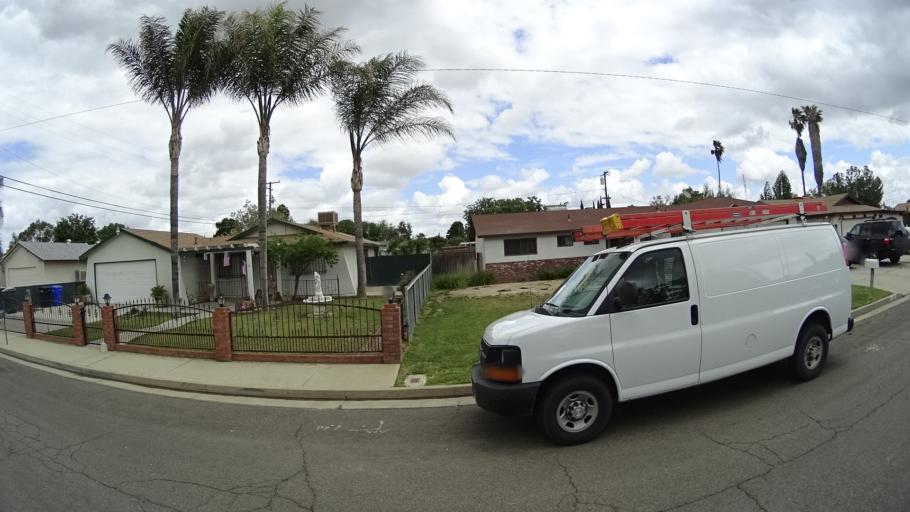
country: US
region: California
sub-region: Kings County
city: Hanford
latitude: 36.3321
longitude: -119.6295
